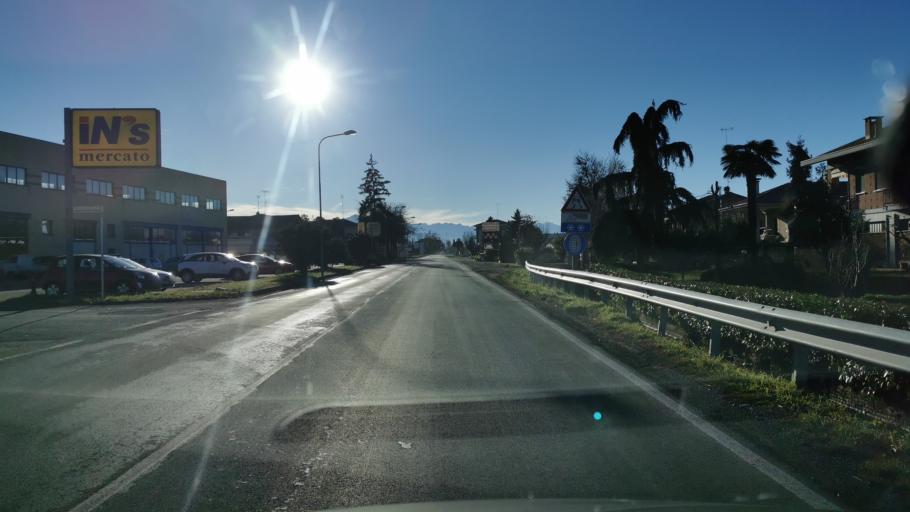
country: IT
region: Piedmont
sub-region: Provincia di Cuneo
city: Carru
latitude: 44.4770
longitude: 7.8648
